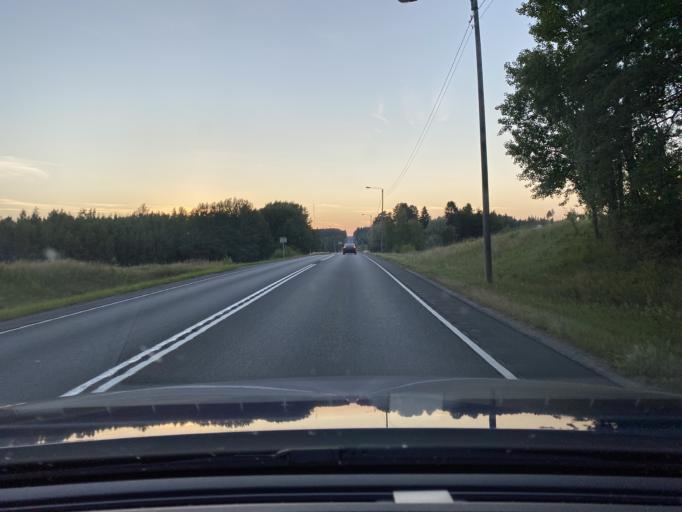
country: FI
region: Pirkanmaa
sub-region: Luoteis-Pirkanmaa
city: Ikaalinen
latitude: 61.7716
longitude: 23.0122
